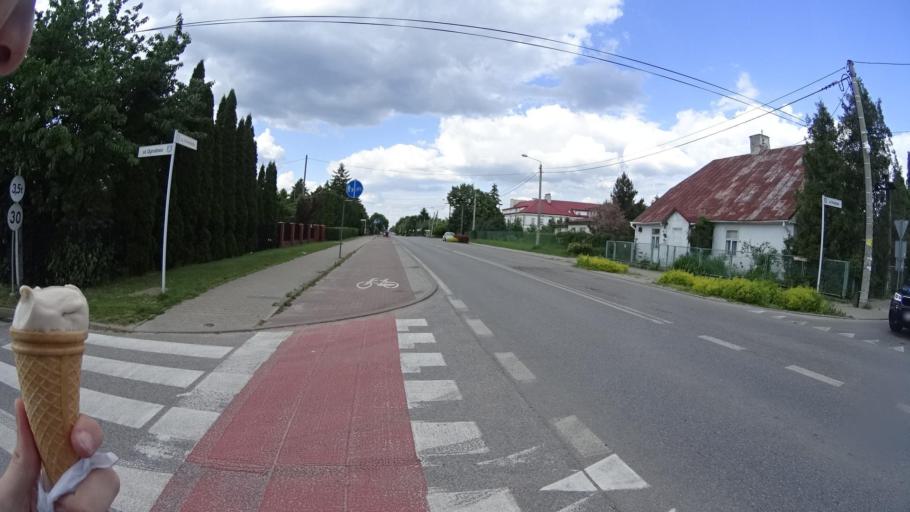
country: PL
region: Masovian Voivodeship
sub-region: Powiat piaseczynski
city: Tarczyn
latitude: 51.9848
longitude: 20.8356
